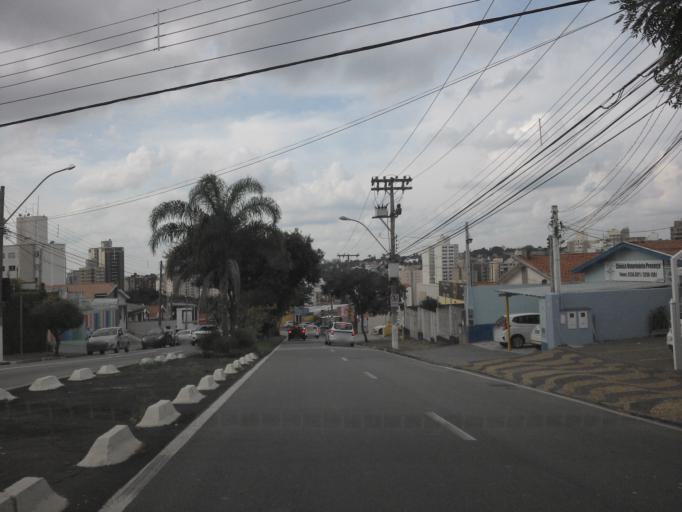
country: BR
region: Sao Paulo
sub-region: Campinas
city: Campinas
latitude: -22.9160
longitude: -47.0490
